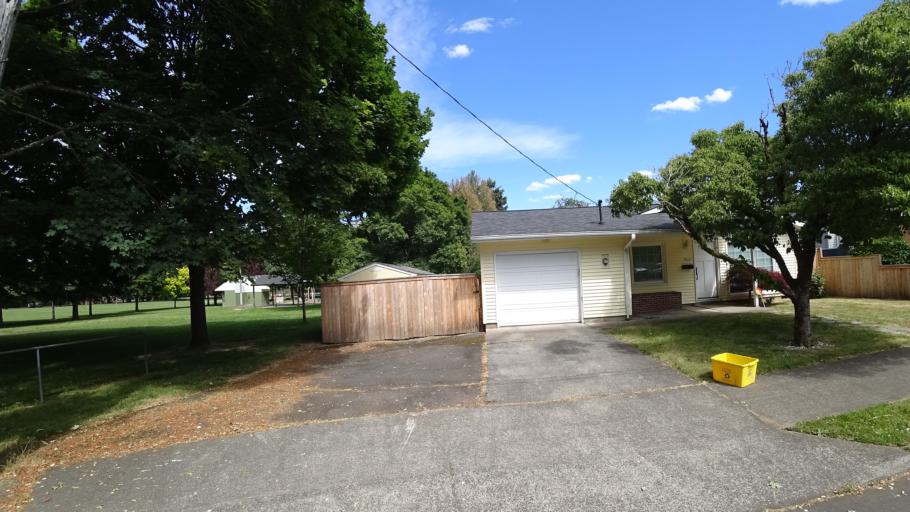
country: US
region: Washington
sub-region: Clark County
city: Vancouver
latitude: 45.5894
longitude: -122.7263
